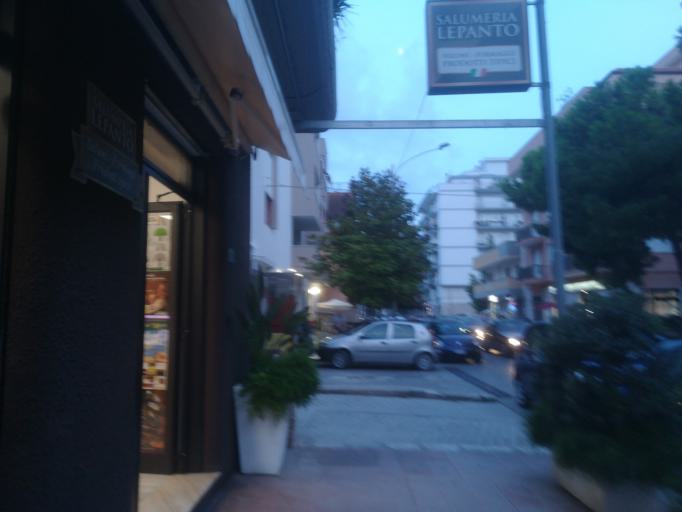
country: IT
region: Apulia
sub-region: Provincia di Bari
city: Monopoli
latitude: 40.9484
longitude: 17.3033
